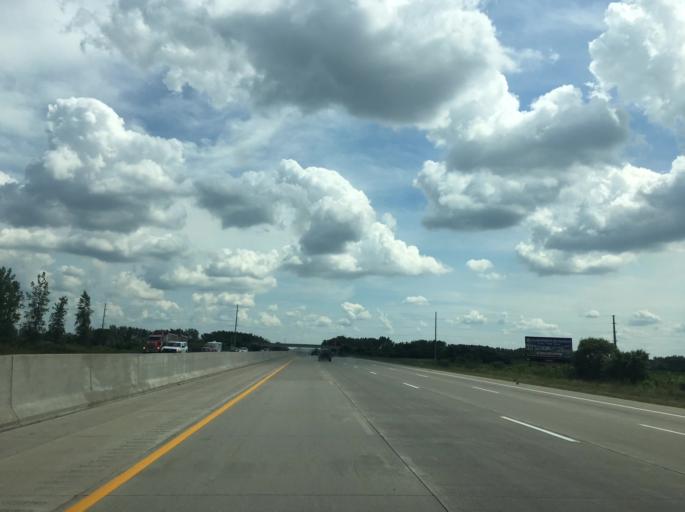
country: US
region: Michigan
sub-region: Saginaw County
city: Zilwaukee
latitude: 43.5149
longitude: -83.9369
